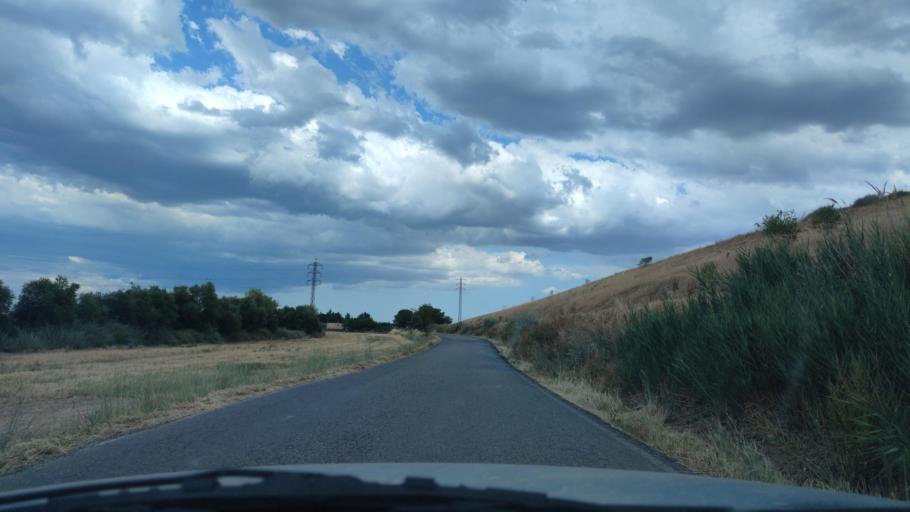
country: ES
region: Catalonia
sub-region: Provincia de Lleida
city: Lleida
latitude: 41.6170
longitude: 0.5749
